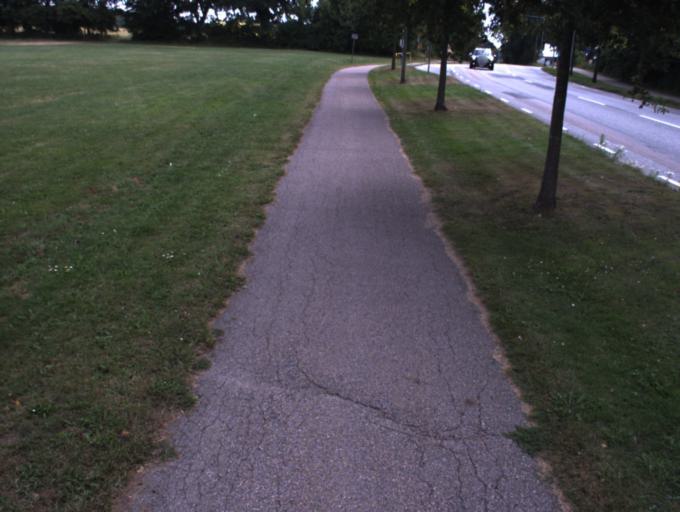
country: SE
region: Skane
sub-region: Helsingborg
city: Helsingborg
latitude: 56.0806
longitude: 12.6635
